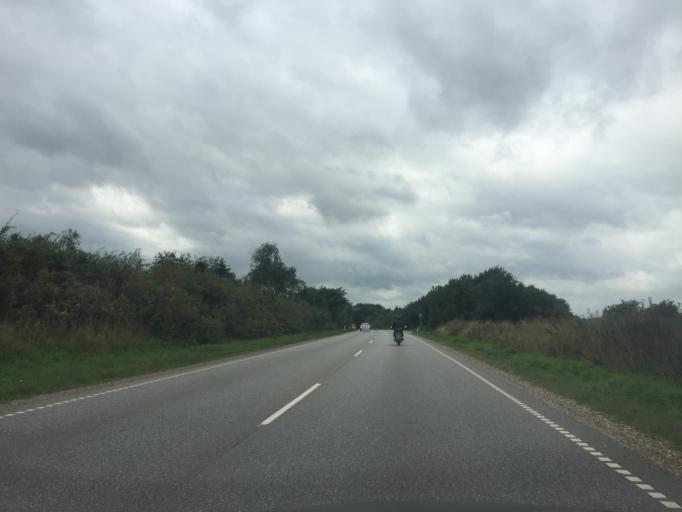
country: DK
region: Capital Region
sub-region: Hillerod Kommune
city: Skaevinge
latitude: 55.9377
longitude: 12.1225
